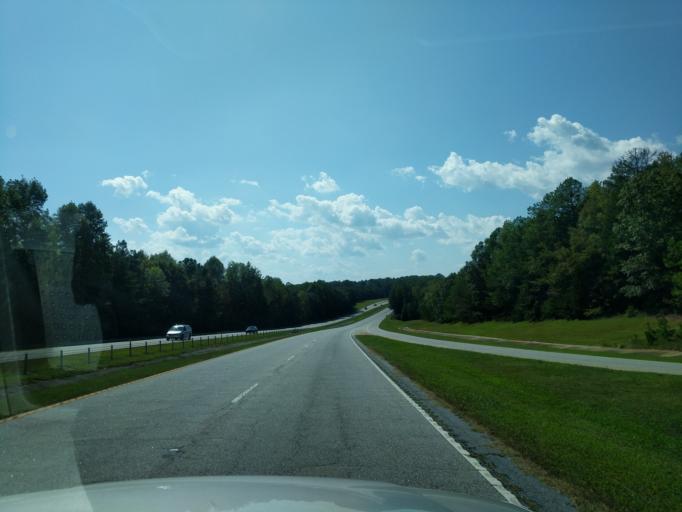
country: US
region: South Carolina
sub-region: Anderson County
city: Pendleton
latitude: 34.6877
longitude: -82.7898
